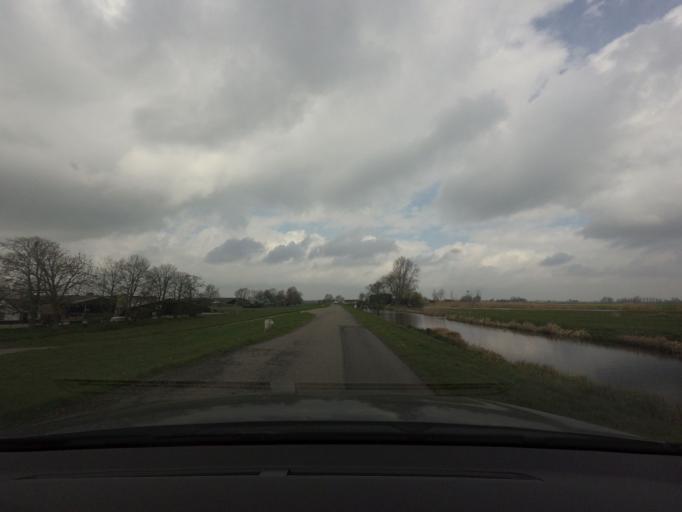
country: NL
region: North Holland
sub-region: Gemeente Uithoorn
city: Uithoorn
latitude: 52.1940
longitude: 4.8092
